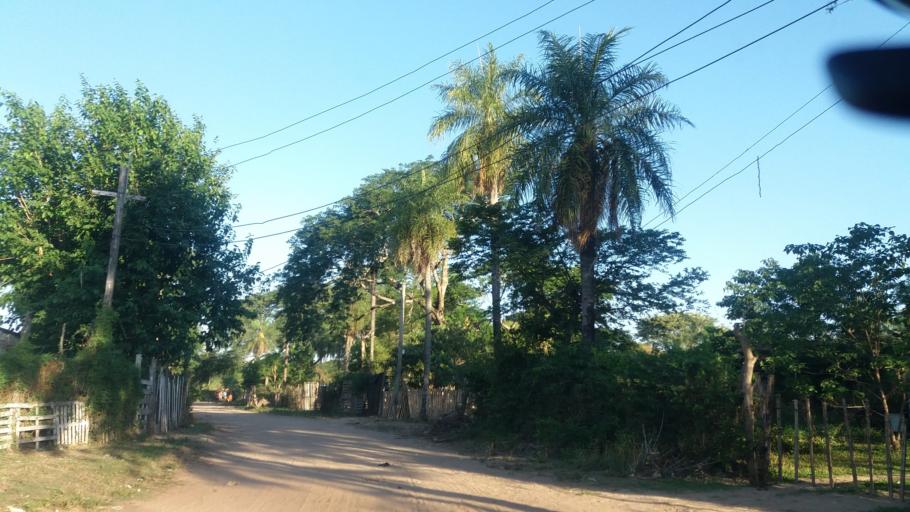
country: AR
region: Corrientes
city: Corrientes
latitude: -27.5215
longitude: -58.8274
